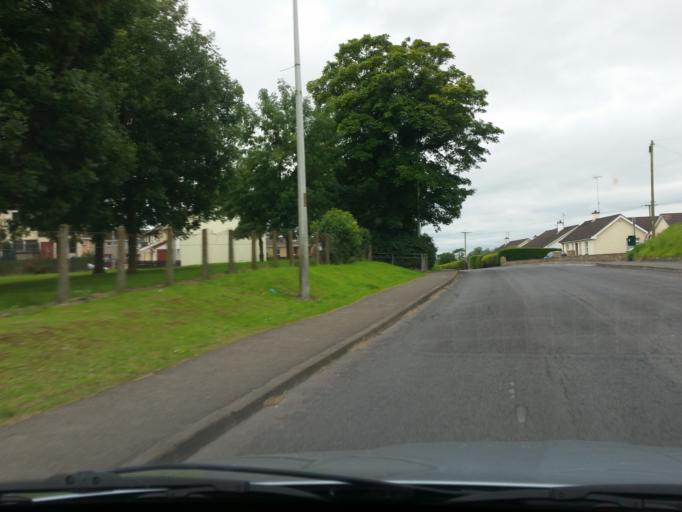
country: GB
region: Northern Ireland
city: Lisnaskea
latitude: 54.2498
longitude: -7.4472
